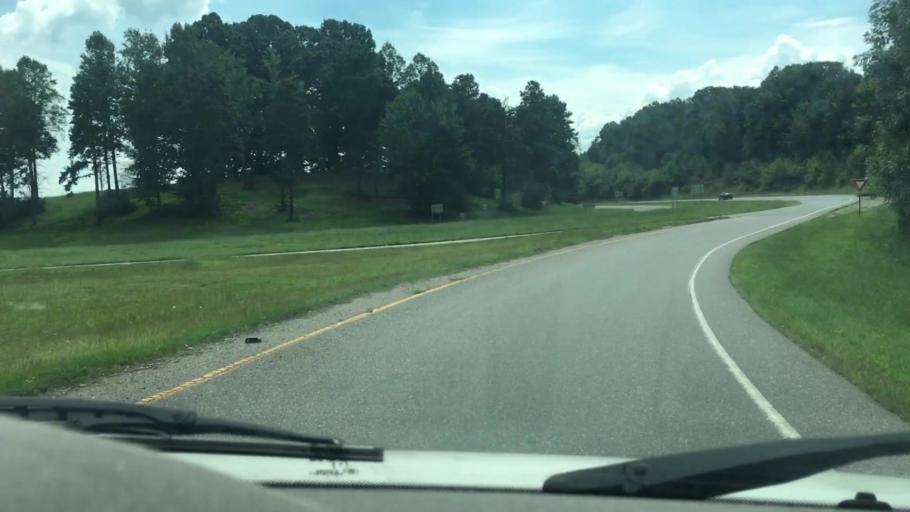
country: US
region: North Carolina
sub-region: Iredell County
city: Troutman
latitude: 35.6758
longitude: -80.8578
